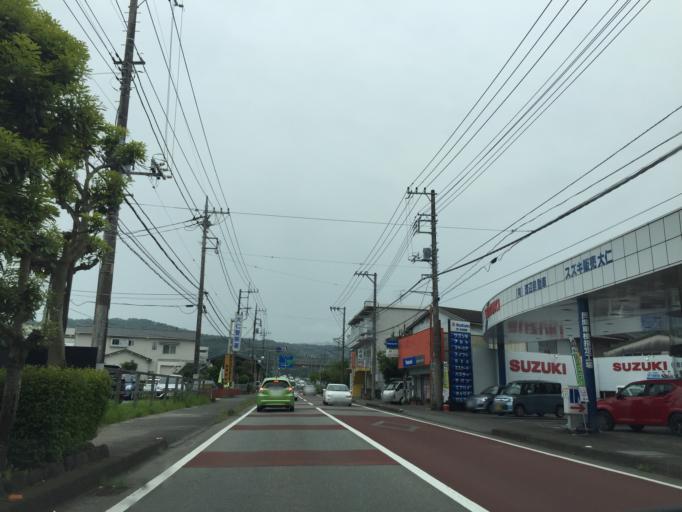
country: JP
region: Shizuoka
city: Mishima
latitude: 34.9983
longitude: 138.9376
